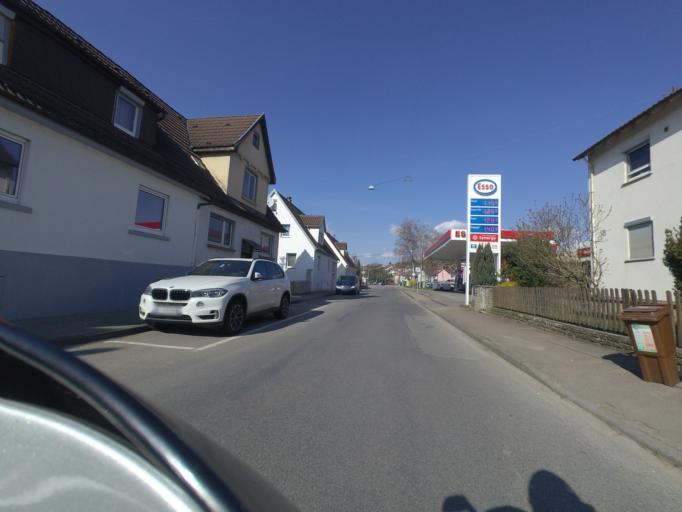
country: DE
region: Baden-Wuerttemberg
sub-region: Regierungsbezirk Stuttgart
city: Oberboihingen
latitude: 48.6537
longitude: 9.3660
